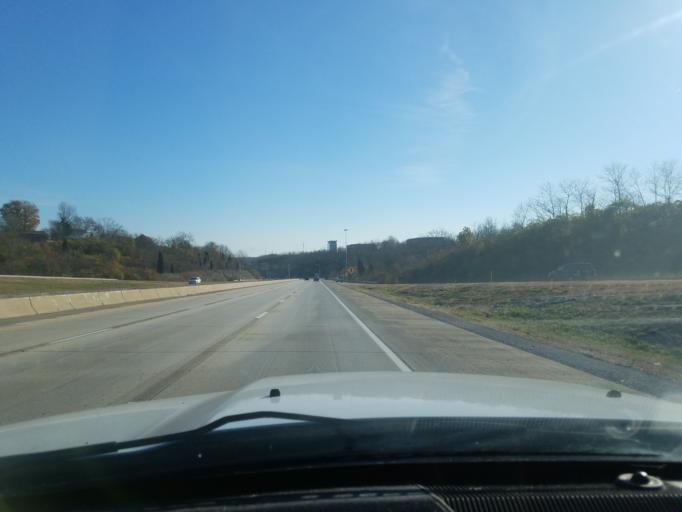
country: US
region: Kentucky
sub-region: Kenton County
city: Lakeside Park
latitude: 39.0258
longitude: -84.5658
